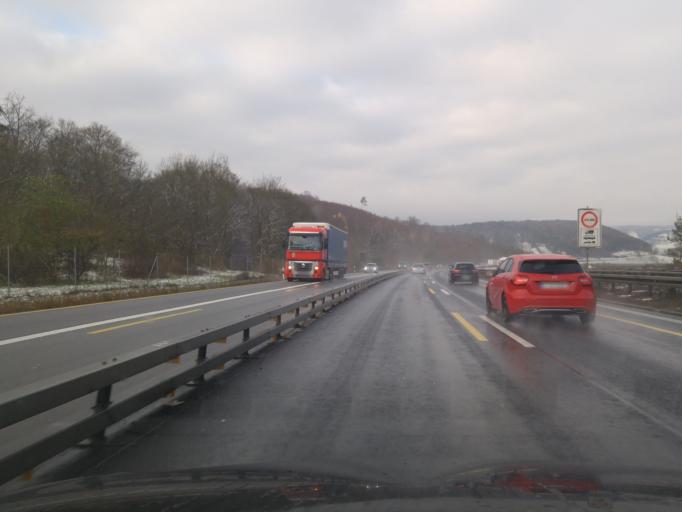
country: DE
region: Bavaria
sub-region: Regierungsbezirk Unterfranken
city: Fuchsstadt
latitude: 50.1053
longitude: 9.9653
